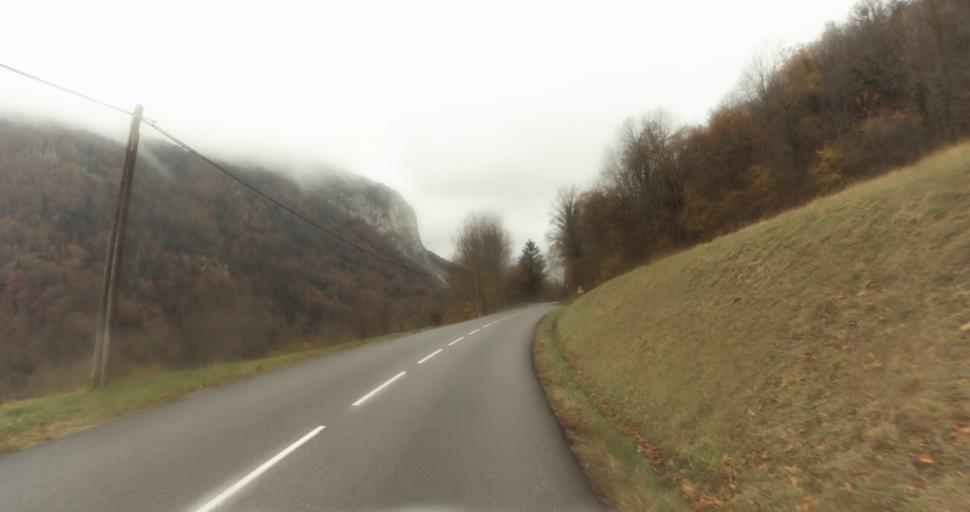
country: FR
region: Rhone-Alpes
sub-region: Departement de la Haute-Savoie
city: Thorens-Glieres
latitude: 45.9859
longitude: 6.2766
